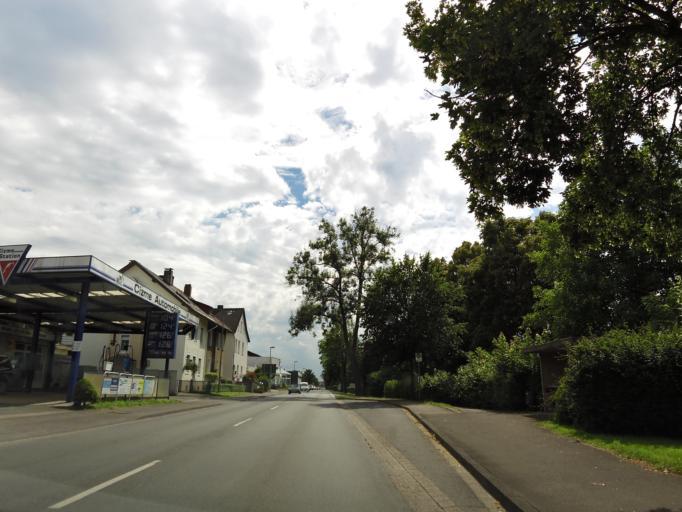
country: DE
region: Lower Saxony
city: Boffzen
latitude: 51.7597
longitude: 9.4058
